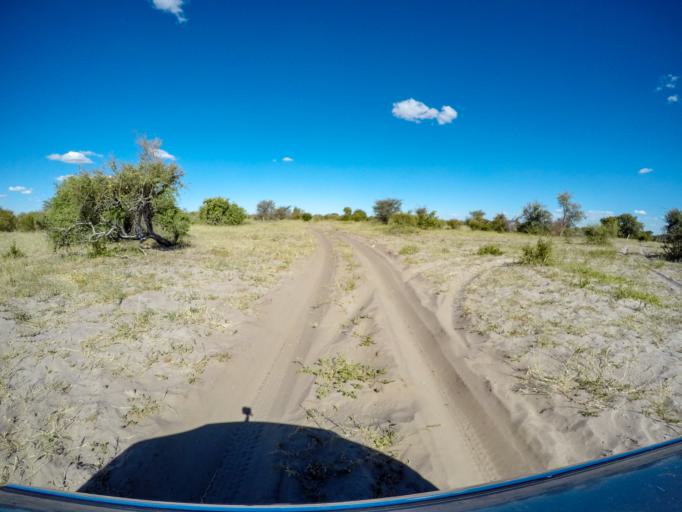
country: BW
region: Central
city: Rakops
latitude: -20.3912
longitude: 24.5149
